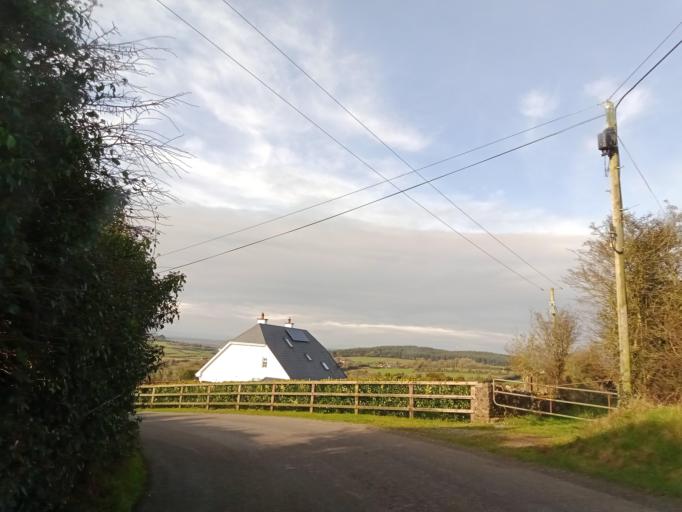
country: IE
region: Munster
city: Fethard
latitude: 52.5700
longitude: -7.6598
